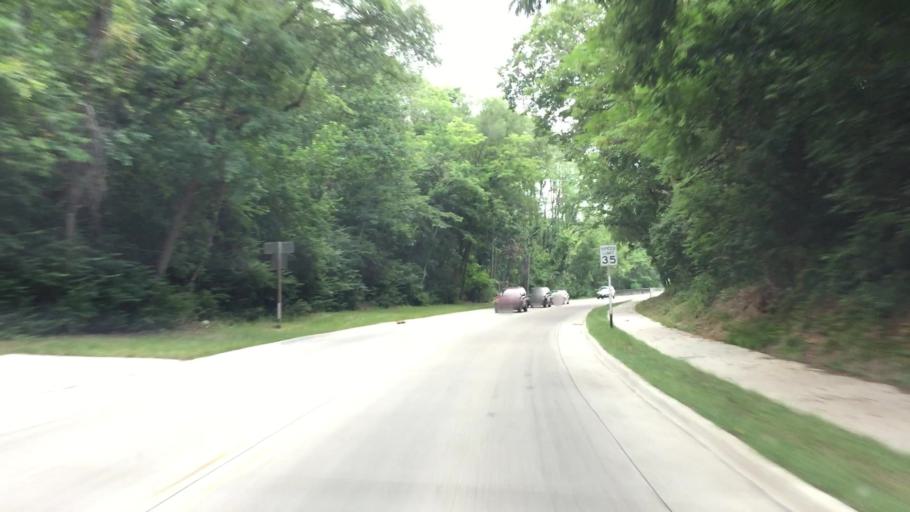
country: US
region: Iowa
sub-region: Lee County
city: Fort Madison
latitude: 40.6380
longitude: -91.3243
